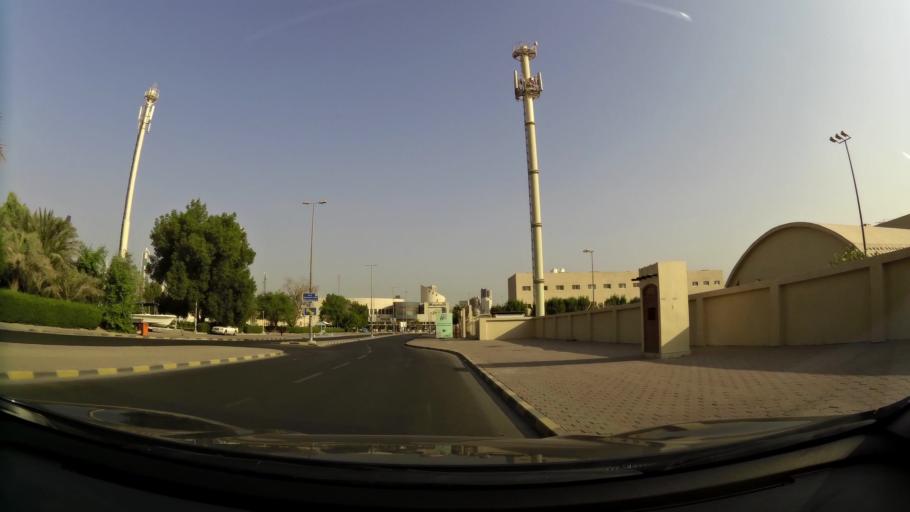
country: KW
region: Al Asimah
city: Ad Dasmah
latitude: 29.3634
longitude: 48.0013
